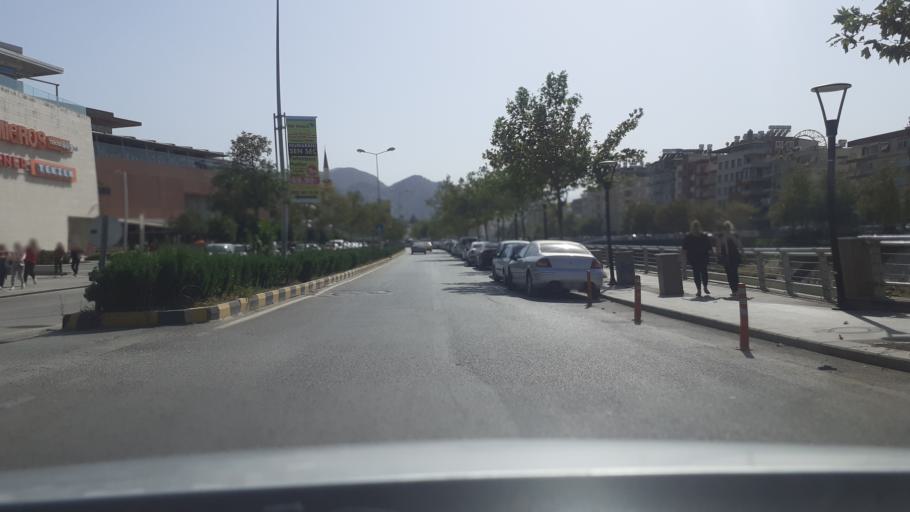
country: TR
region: Hatay
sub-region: Antakya Ilcesi
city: Antakya
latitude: 36.2097
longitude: 36.1623
